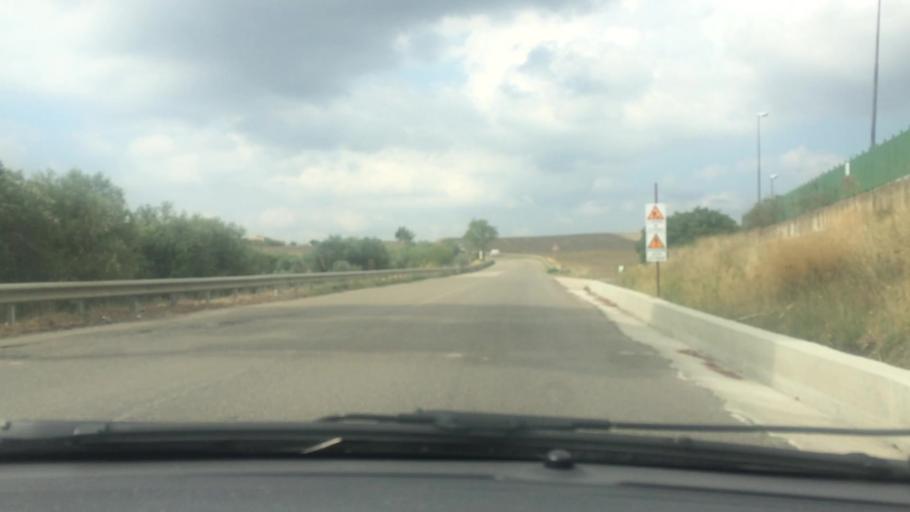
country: IT
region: Basilicate
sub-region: Provincia di Matera
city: La Martella
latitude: 40.6882
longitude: 16.5606
